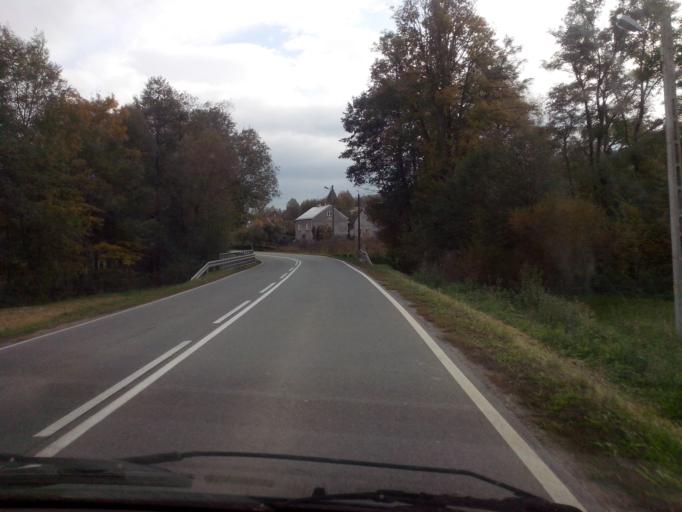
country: PL
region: Subcarpathian Voivodeship
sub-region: Powiat strzyzowski
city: Wisniowa
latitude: 49.8899
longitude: 21.6437
